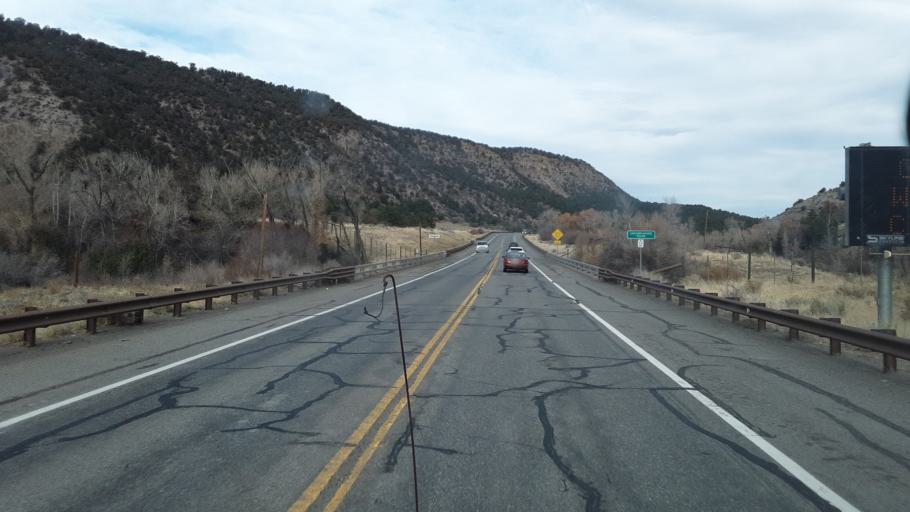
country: US
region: Colorado
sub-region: Montrose County
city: Montrose
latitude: 38.2663
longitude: -107.7607
